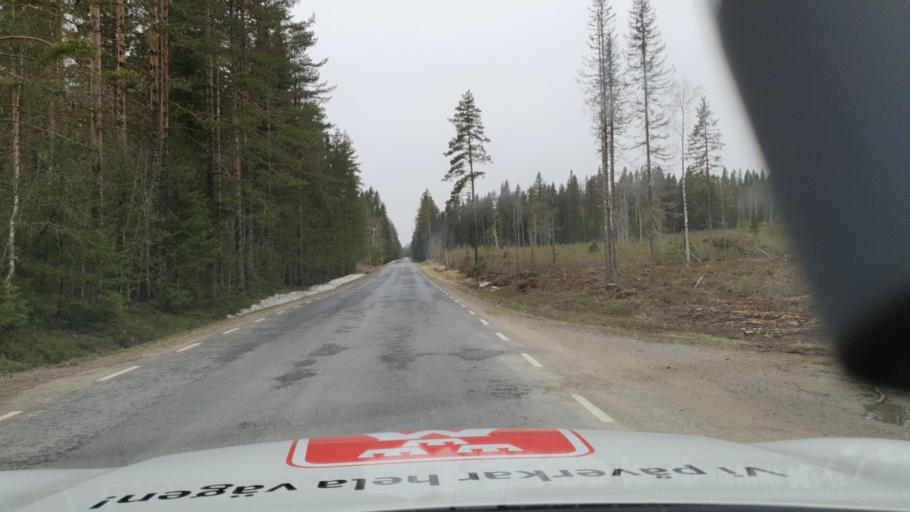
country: SE
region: Vaesterbotten
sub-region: Nordmalings Kommun
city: Nordmaling
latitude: 63.7207
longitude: 19.5570
